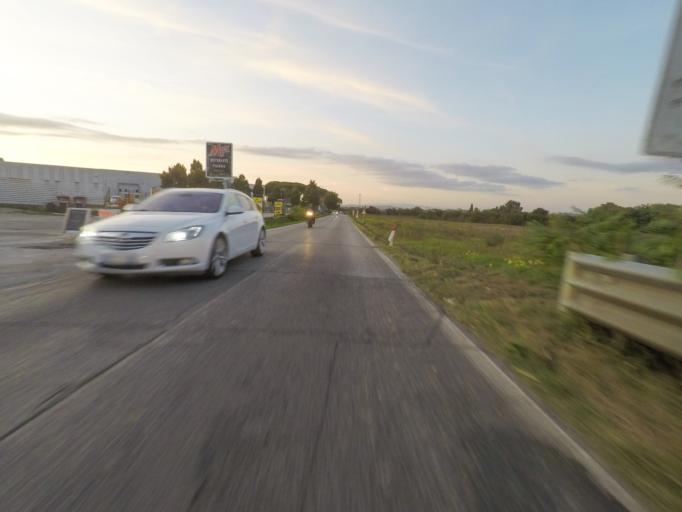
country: IT
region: Tuscany
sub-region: Provincia di Siena
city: Torrita di Siena
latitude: 43.1808
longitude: 11.7709
